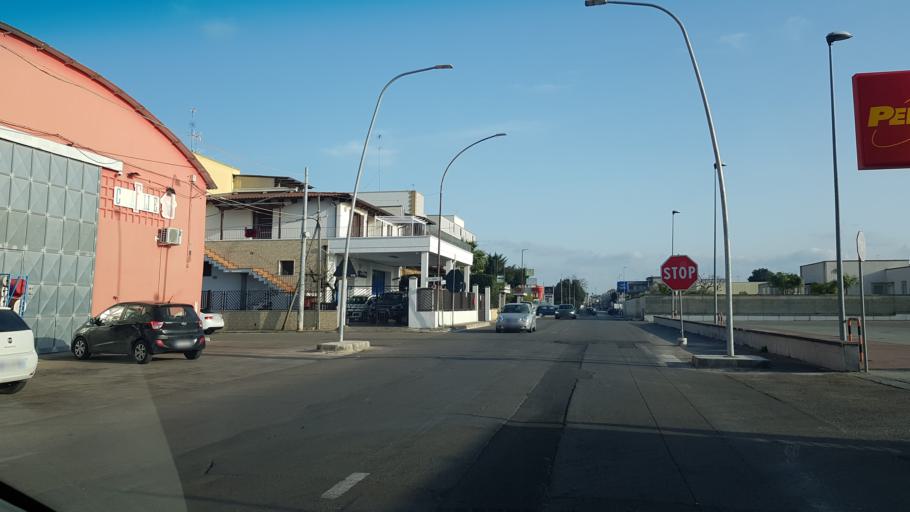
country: IT
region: Apulia
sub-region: Provincia di Lecce
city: Trepuzzi
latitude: 40.4121
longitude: 18.0653
